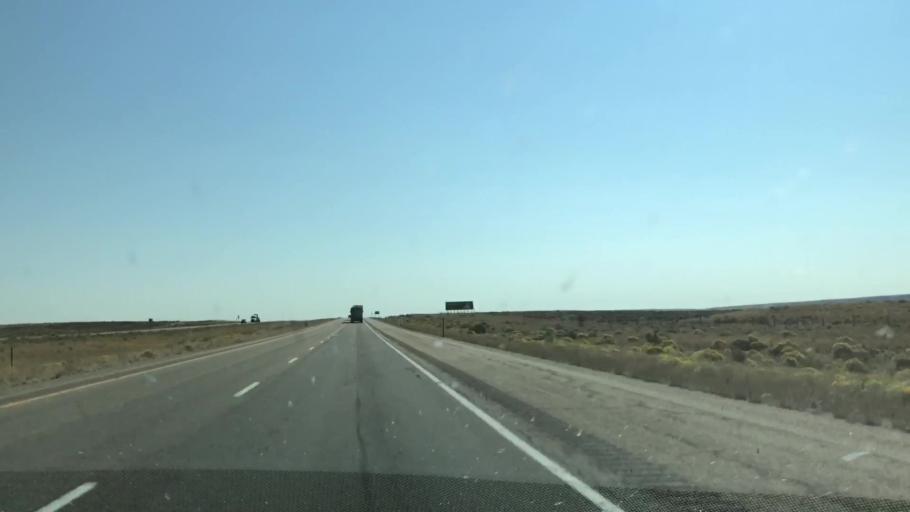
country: US
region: Wyoming
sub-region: Sweetwater County
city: Rock Springs
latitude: 41.6340
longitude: -108.3923
